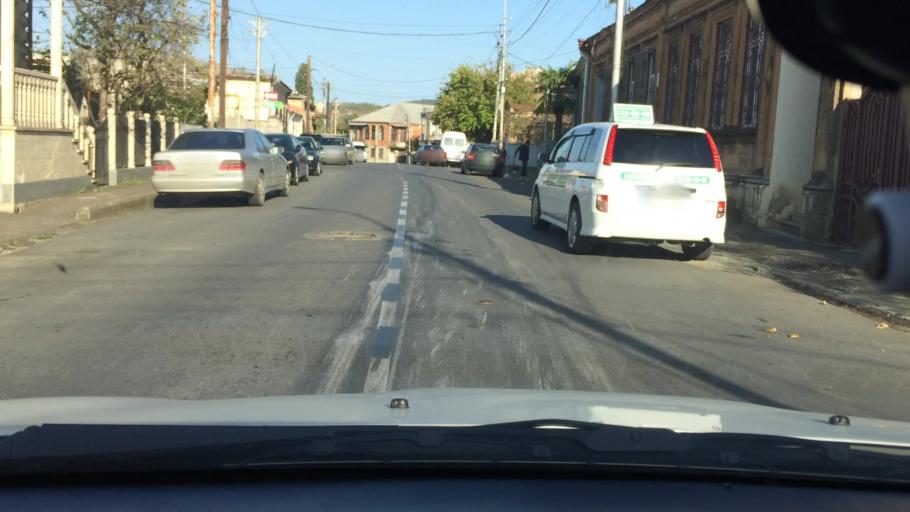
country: GE
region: Imereti
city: Kutaisi
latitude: 42.2716
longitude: 42.7127
